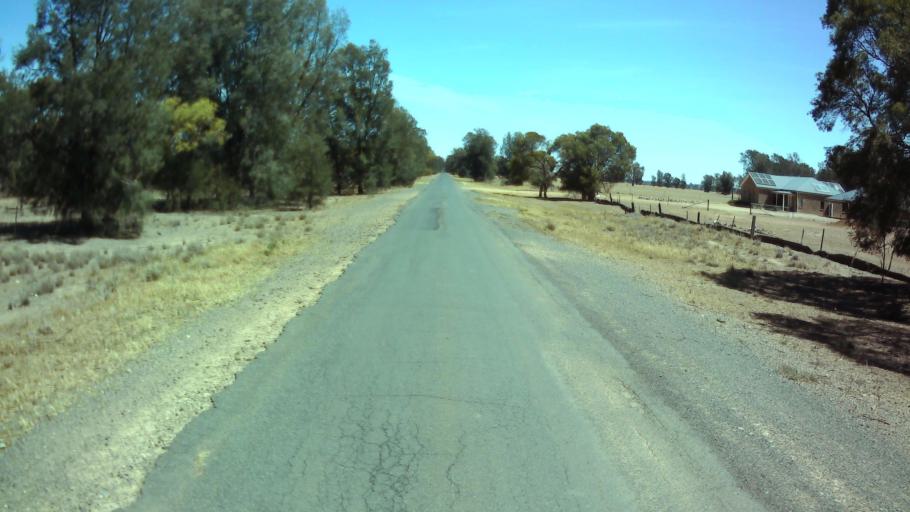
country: AU
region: New South Wales
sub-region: Weddin
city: Grenfell
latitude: -33.8726
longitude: 147.6916
